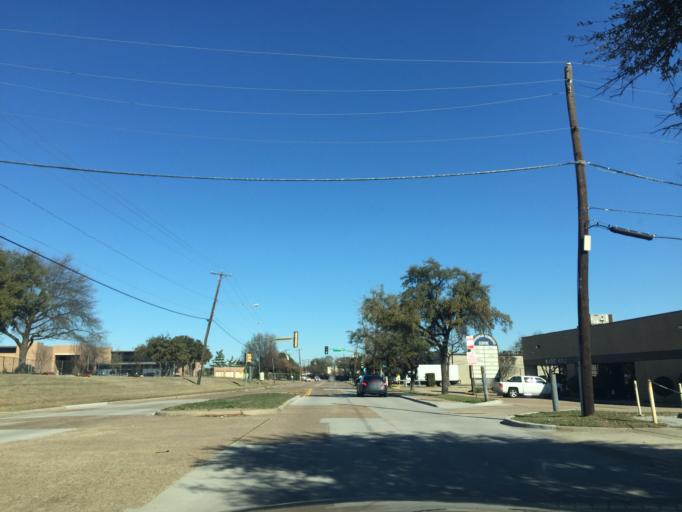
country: US
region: Texas
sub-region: Dallas County
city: Richardson
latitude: 32.9331
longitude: -96.7485
